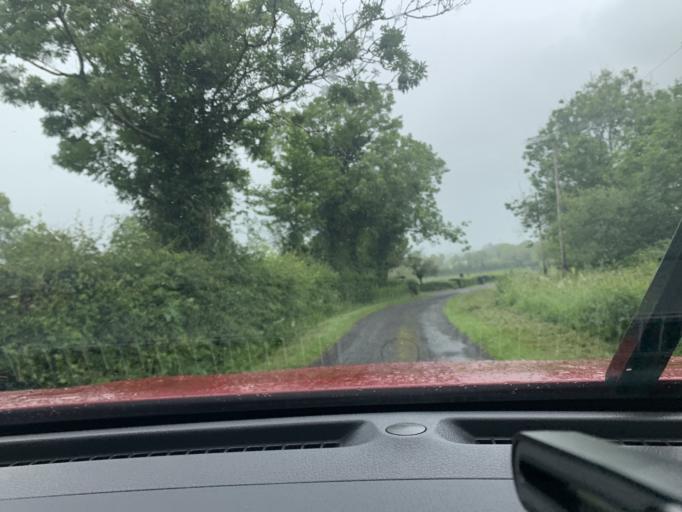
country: GB
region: Northern Ireland
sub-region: Fermanagh District
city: Enniskillen
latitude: 54.2685
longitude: -7.7434
